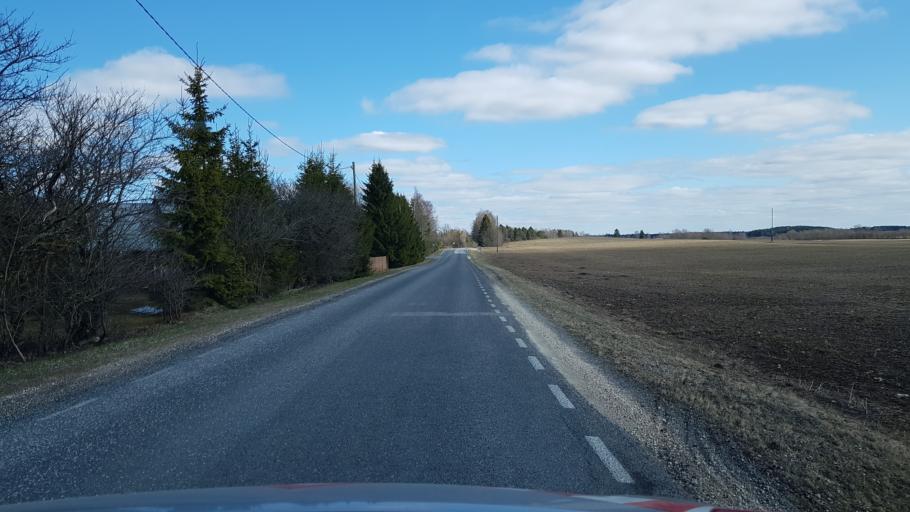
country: EE
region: Laeaene-Virumaa
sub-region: Tapa vald
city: Tapa
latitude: 59.2538
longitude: 25.7064
